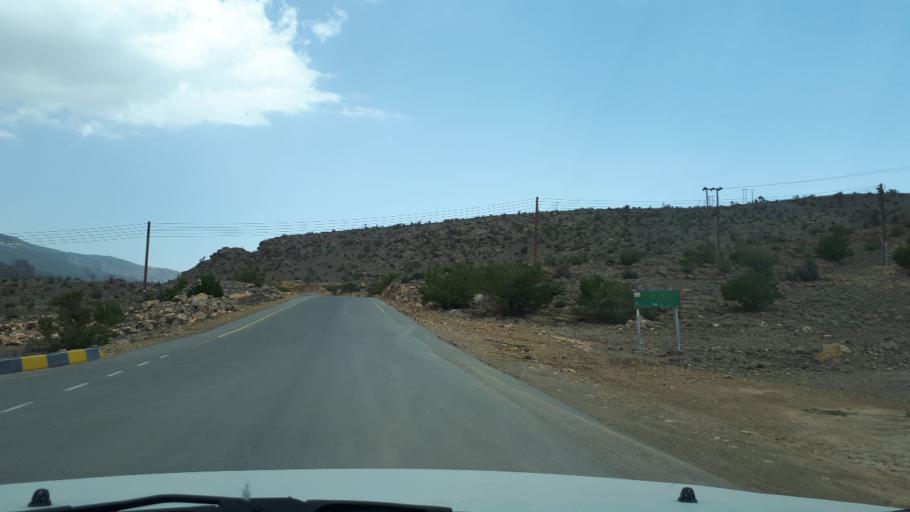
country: OM
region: Muhafazat ad Dakhiliyah
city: Bahla'
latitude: 23.2267
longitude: 57.2010
